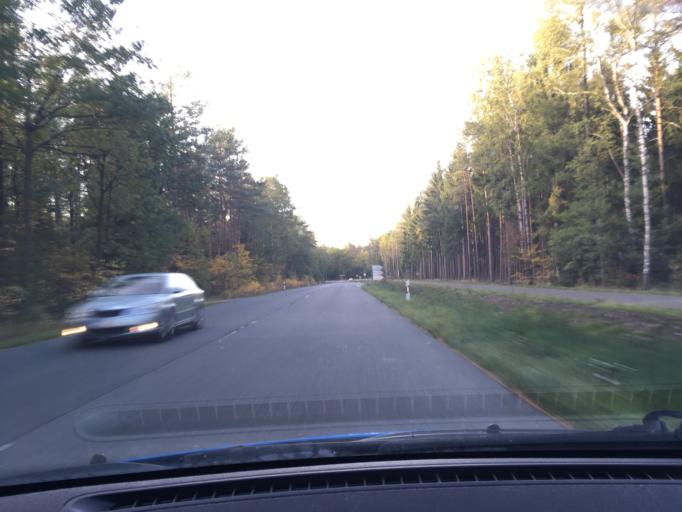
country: DE
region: Lower Saxony
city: Bispingen
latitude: 53.0539
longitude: 10.0299
